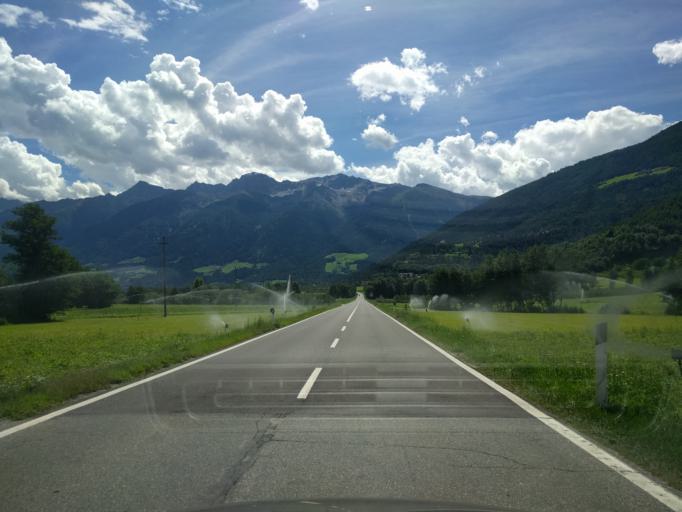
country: IT
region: Trentino-Alto Adige
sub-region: Bolzano
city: Sluderno
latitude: 46.6472
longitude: 10.5679
